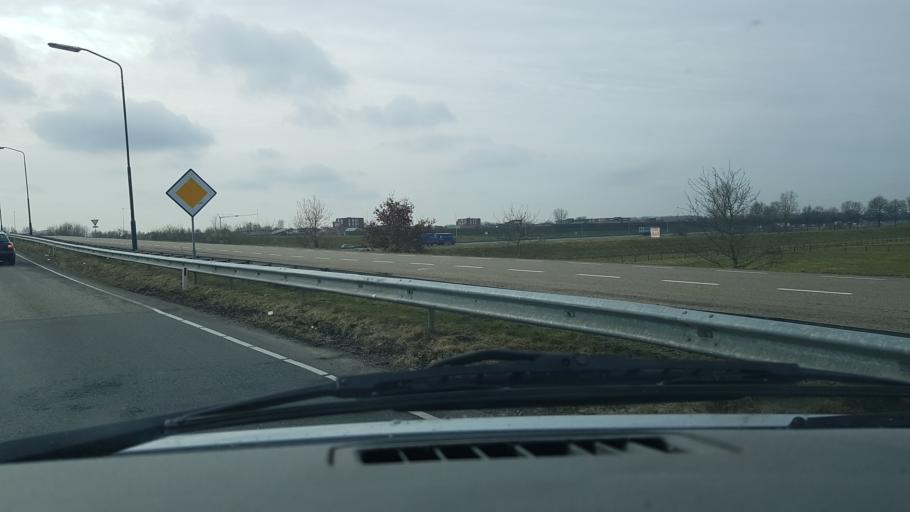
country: NL
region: North Brabant
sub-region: Gemeente Veghel
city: Mariaheide
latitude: 51.6395
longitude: 5.5679
